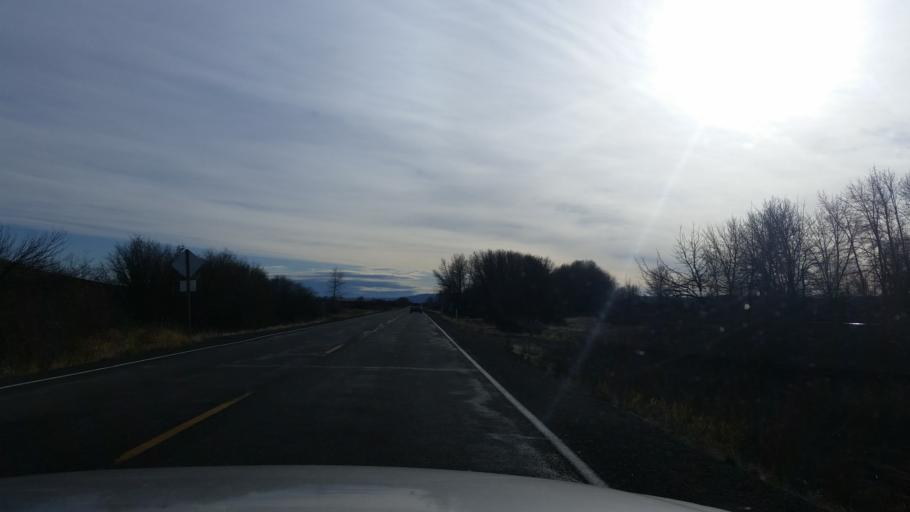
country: US
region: Washington
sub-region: Kittitas County
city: Ellensburg
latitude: 47.0504
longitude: -120.6339
